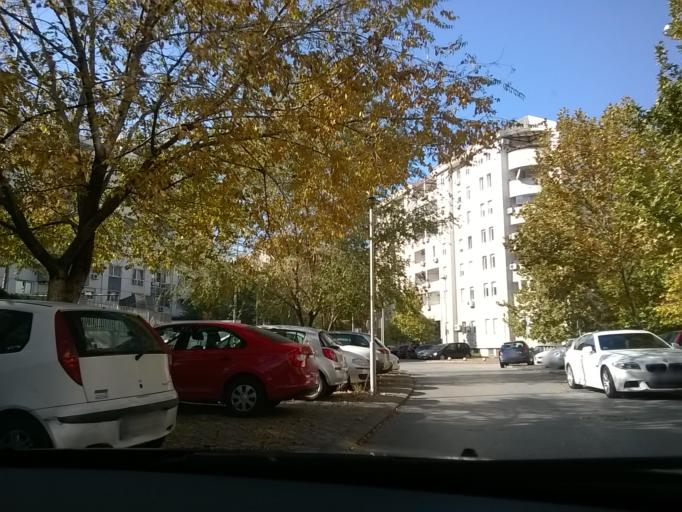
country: RS
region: Central Serbia
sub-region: Belgrade
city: Novi Beograd
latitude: 44.8122
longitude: 20.4268
